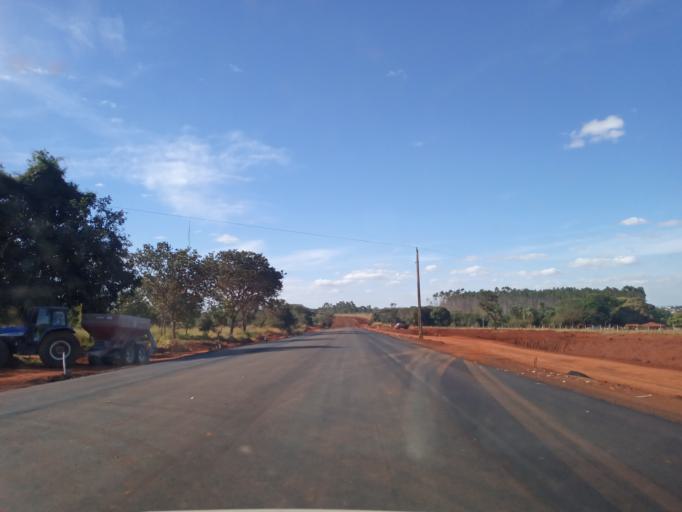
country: BR
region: Minas Gerais
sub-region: Ituiutaba
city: Ituiutaba
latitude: -18.9815
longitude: -49.5093
